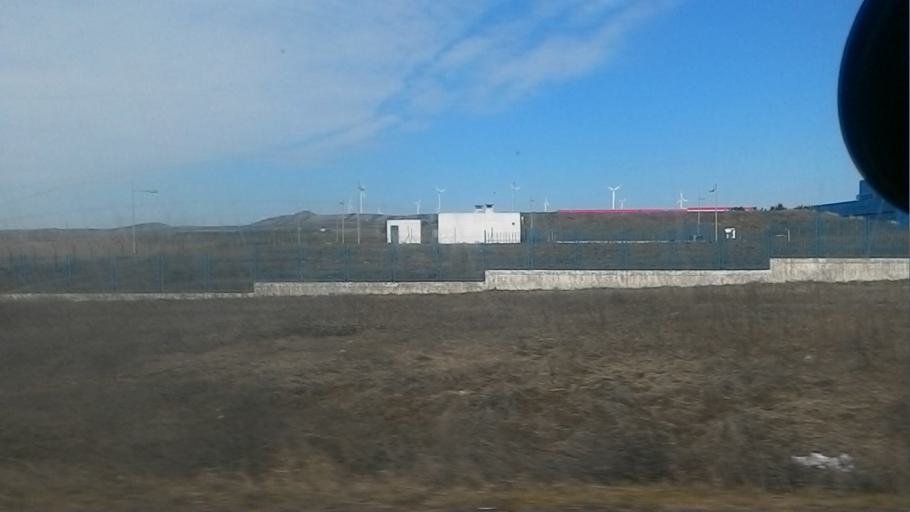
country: TR
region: Istanbul
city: Canta
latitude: 41.0823
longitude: 28.0476
